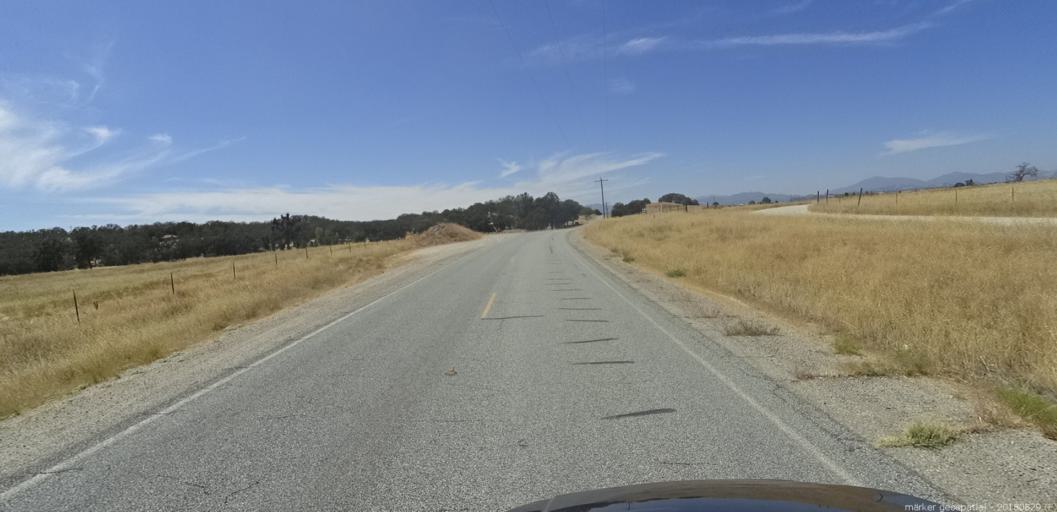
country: US
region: California
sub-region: Monterey County
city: King City
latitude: 35.9371
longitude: -121.1027
